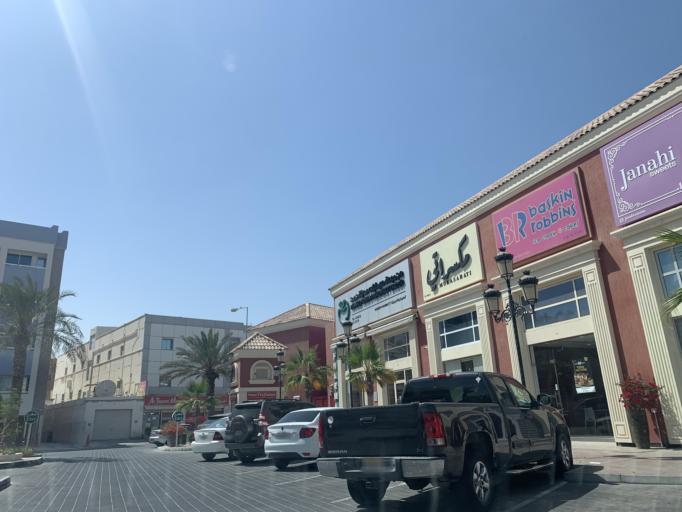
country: BH
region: Manama
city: Manama
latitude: 26.2113
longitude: 50.5721
